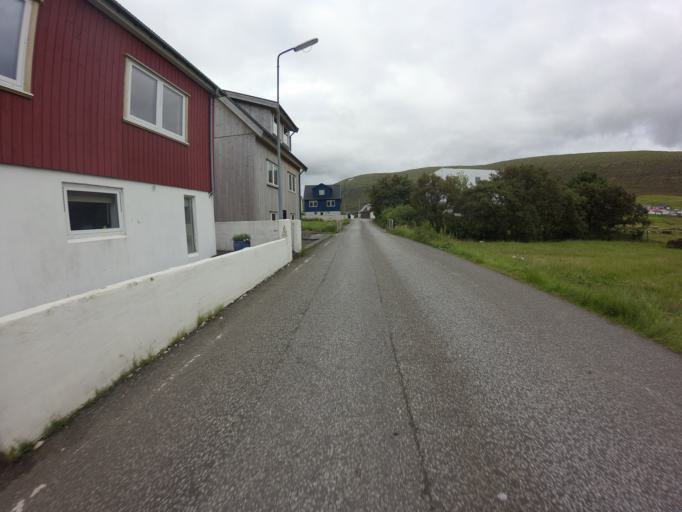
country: FO
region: Eysturoy
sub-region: Eidi
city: Eidi
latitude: 62.1877
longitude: -7.0379
